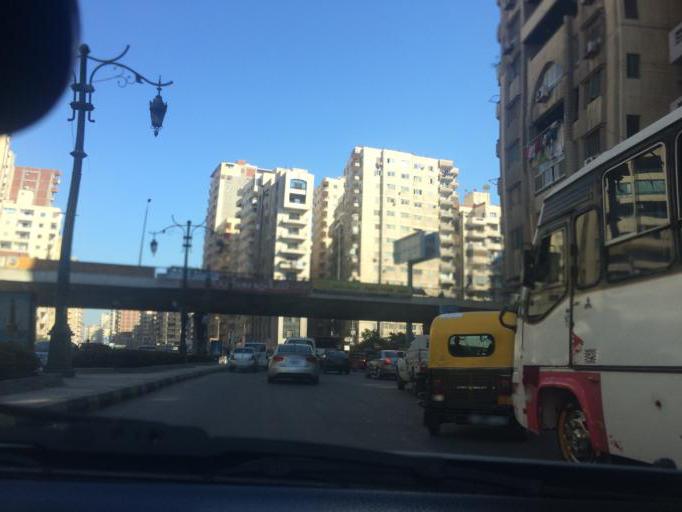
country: EG
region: Alexandria
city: Alexandria
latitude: 31.2680
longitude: 29.9996
